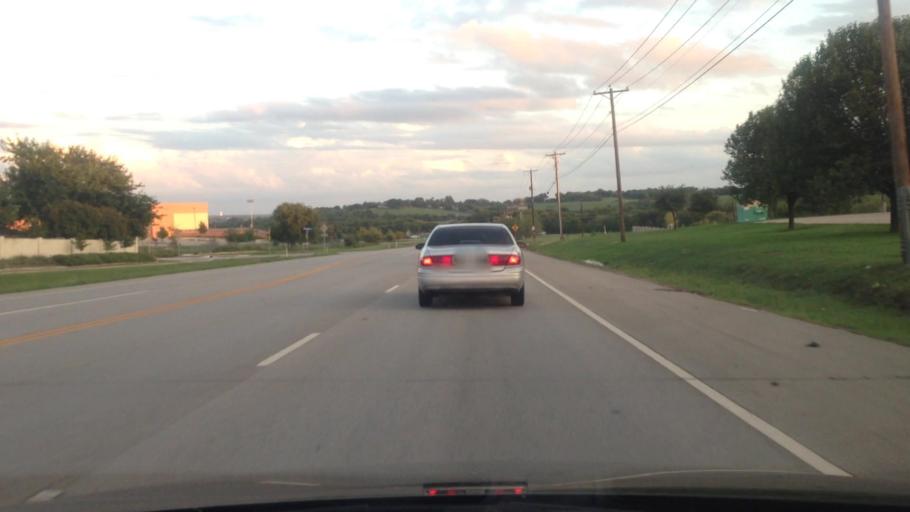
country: US
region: Texas
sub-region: Tarrant County
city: Benbrook
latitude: 32.6664
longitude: -97.4891
